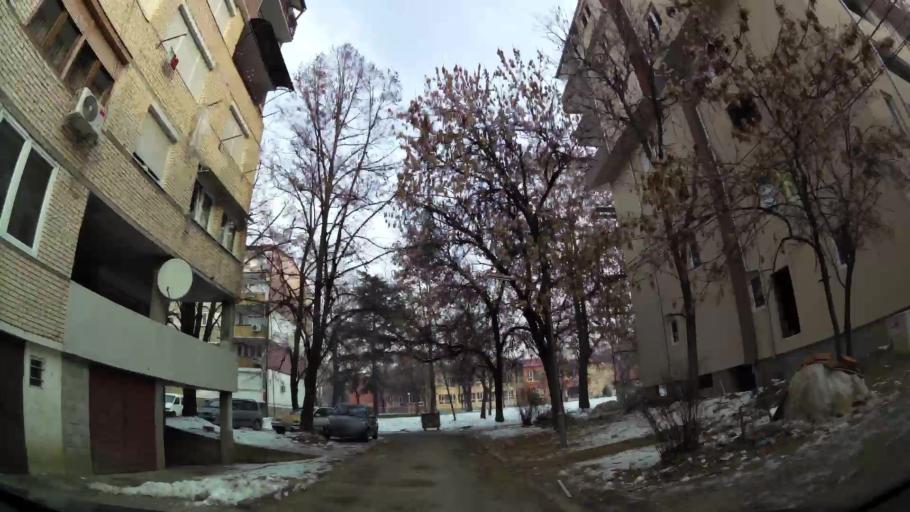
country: MK
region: Cair
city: Cair
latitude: 42.0209
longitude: 21.4423
